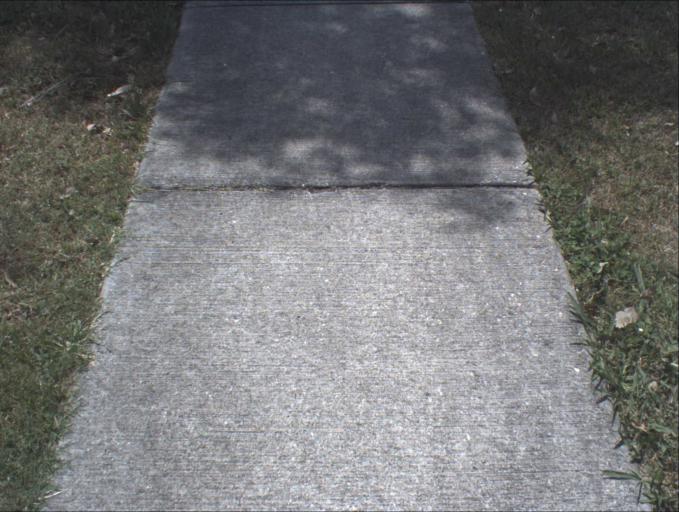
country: AU
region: Queensland
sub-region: Logan
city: Rochedale South
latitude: -27.6055
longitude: 153.1094
